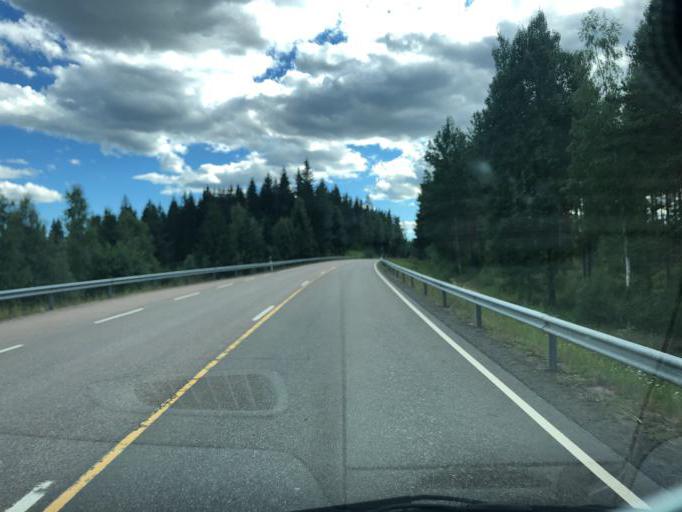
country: FI
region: Southern Savonia
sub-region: Mikkeli
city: Maentyharju
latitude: 61.0630
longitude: 27.0516
